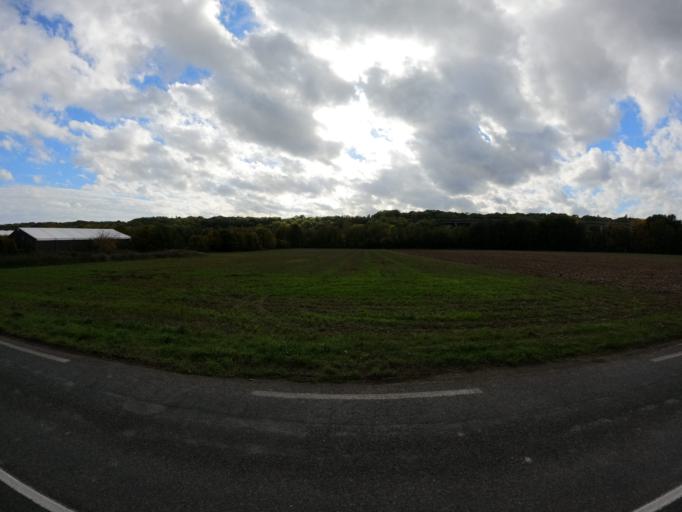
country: FR
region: Ile-de-France
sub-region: Departement de Seine-et-Marne
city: Coupvray
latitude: 48.8993
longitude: 2.7856
